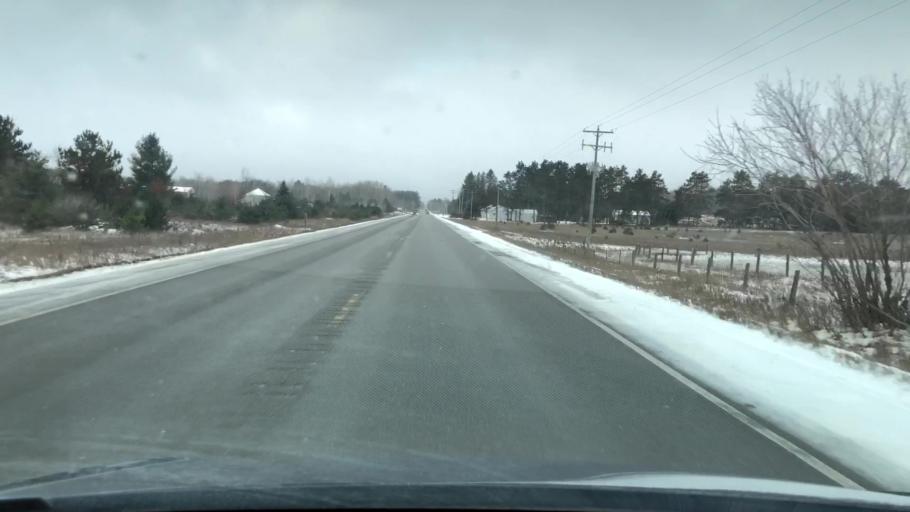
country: US
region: Michigan
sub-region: Wexford County
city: Cadillac
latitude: 44.2813
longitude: -85.4487
